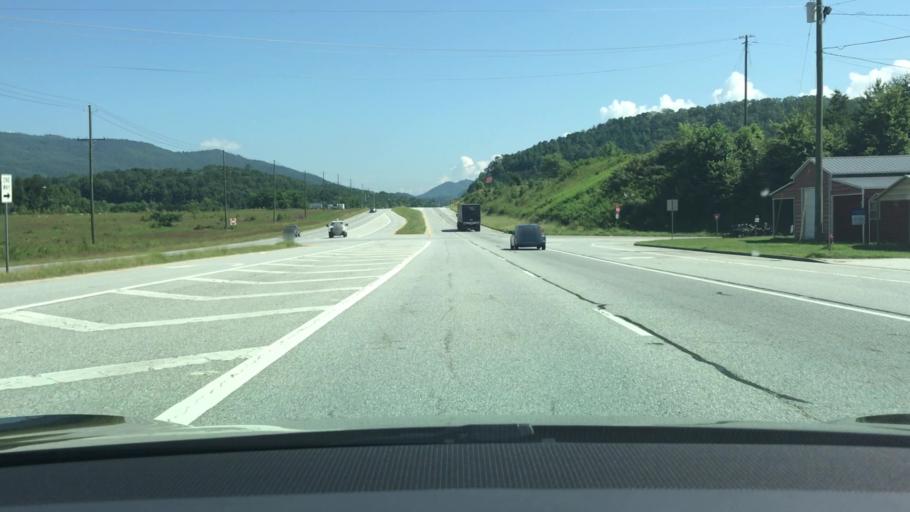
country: US
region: Georgia
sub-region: Rabun County
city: Clayton
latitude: 34.8539
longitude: -83.4084
